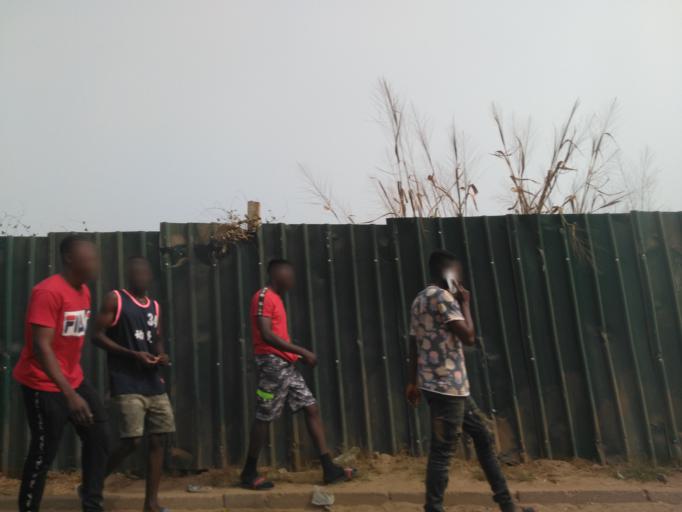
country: GH
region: Ashanti
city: Kumasi
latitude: 6.7085
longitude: -1.6252
